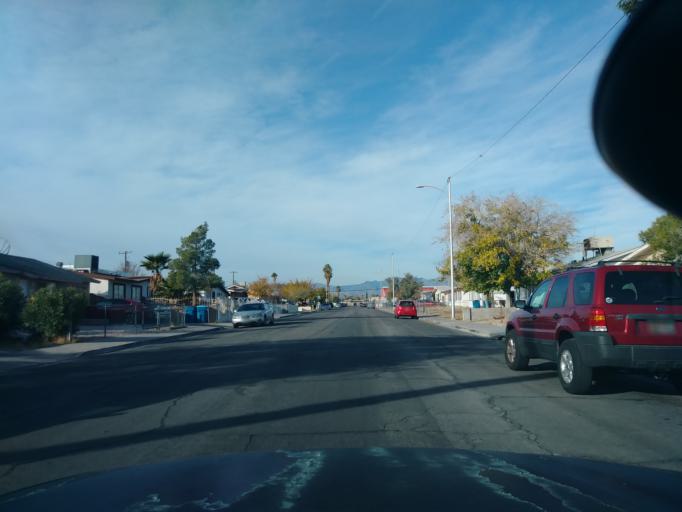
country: US
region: Nevada
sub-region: Clark County
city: Spring Valley
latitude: 36.1636
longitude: -115.2313
